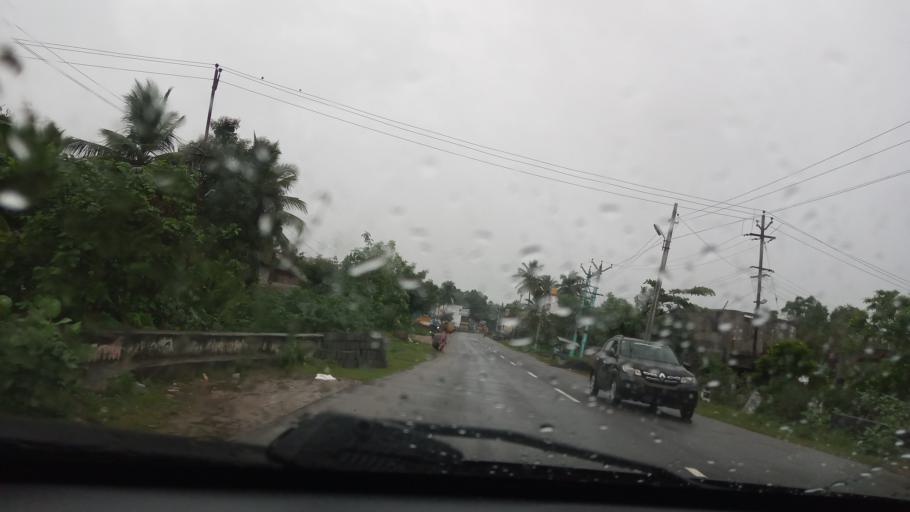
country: IN
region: Tamil Nadu
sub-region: Tiruvannamalai
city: Cheyyar
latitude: 12.6747
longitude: 79.5361
